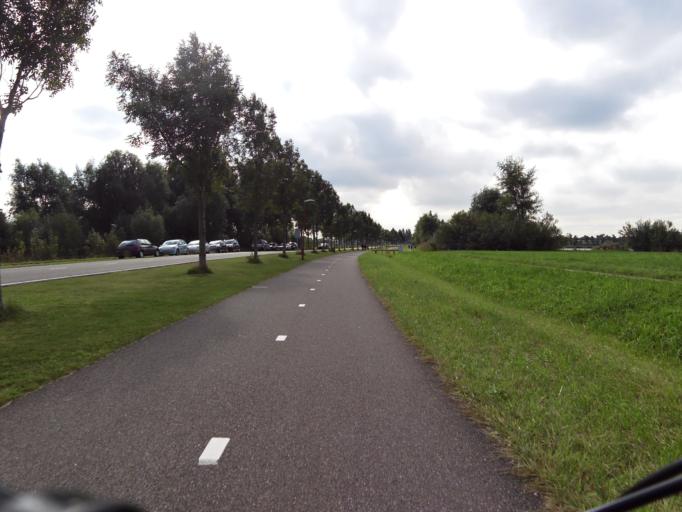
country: NL
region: South Holland
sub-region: Gemeente Rijnwoude
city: Benthuizen
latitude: 52.0838
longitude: 4.5172
